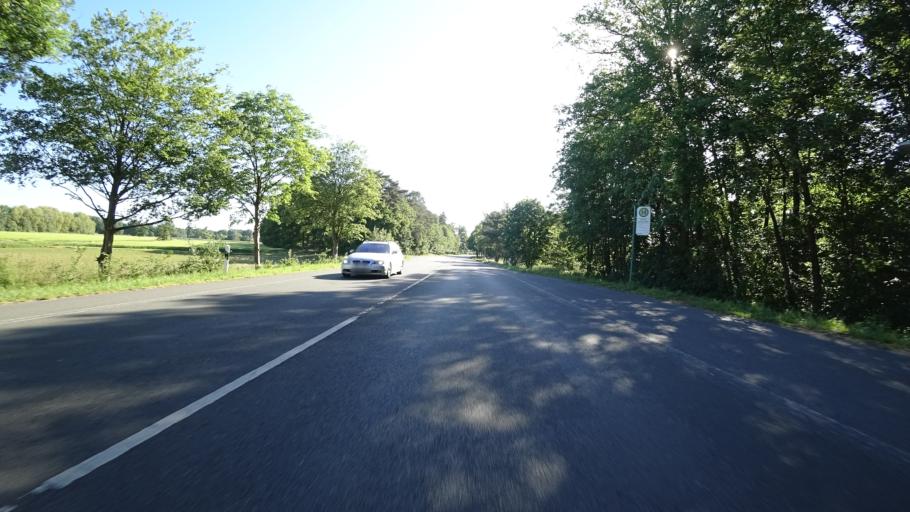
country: DE
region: North Rhine-Westphalia
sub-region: Regierungsbezirk Detmold
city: Rheda-Wiedenbruck
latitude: 51.9003
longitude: 8.3163
